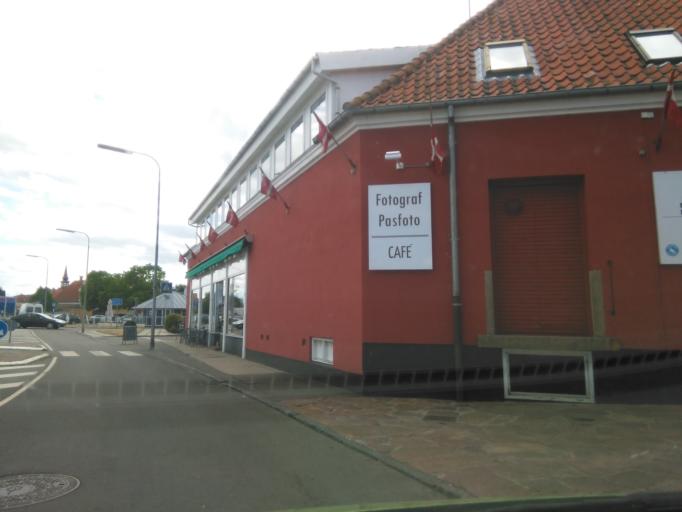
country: DK
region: Capital Region
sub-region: Bornholm Kommune
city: Nexo
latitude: 55.0630
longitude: 15.1341
